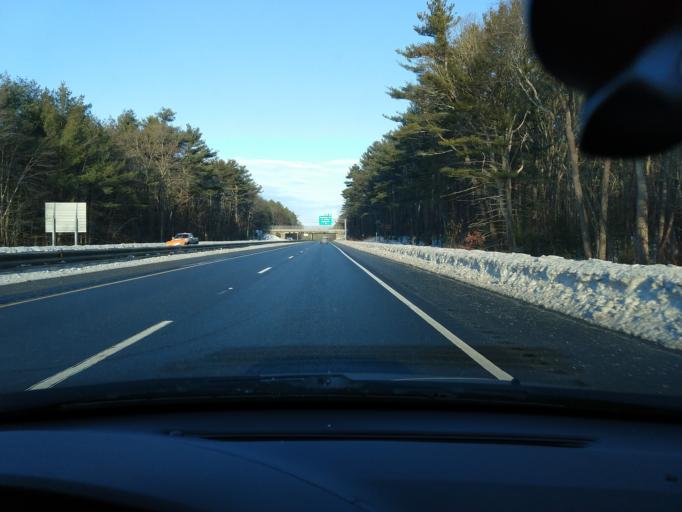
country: US
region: Massachusetts
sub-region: Middlesex County
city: Acton
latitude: 42.4891
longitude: -71.4575
